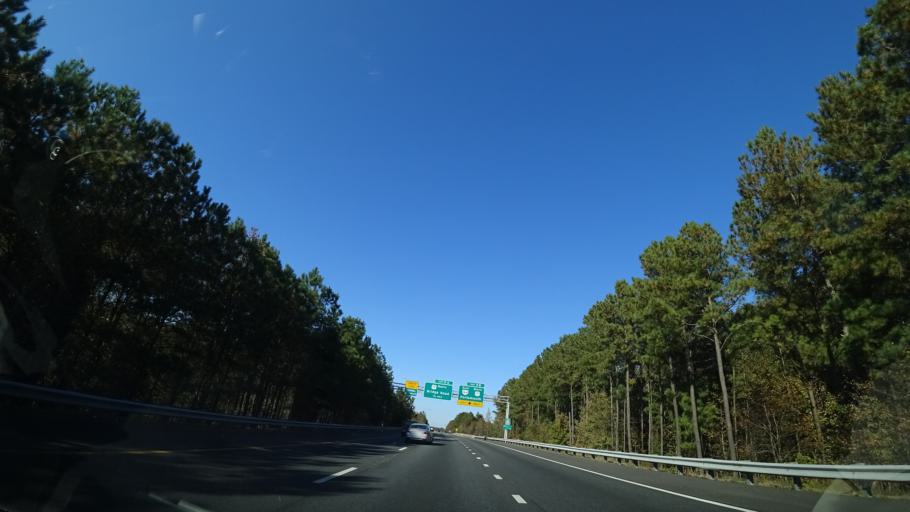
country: US
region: Virginia
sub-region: City of Portsmouth
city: Portsmouth Heights
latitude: 36.8597
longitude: -76.4306
